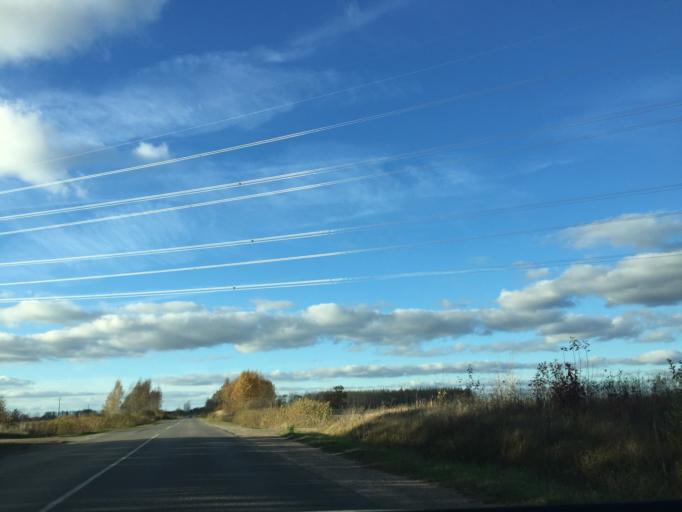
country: LV
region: Tukuma Rajons
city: Tukums
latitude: 56.9826
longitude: 23.1109
